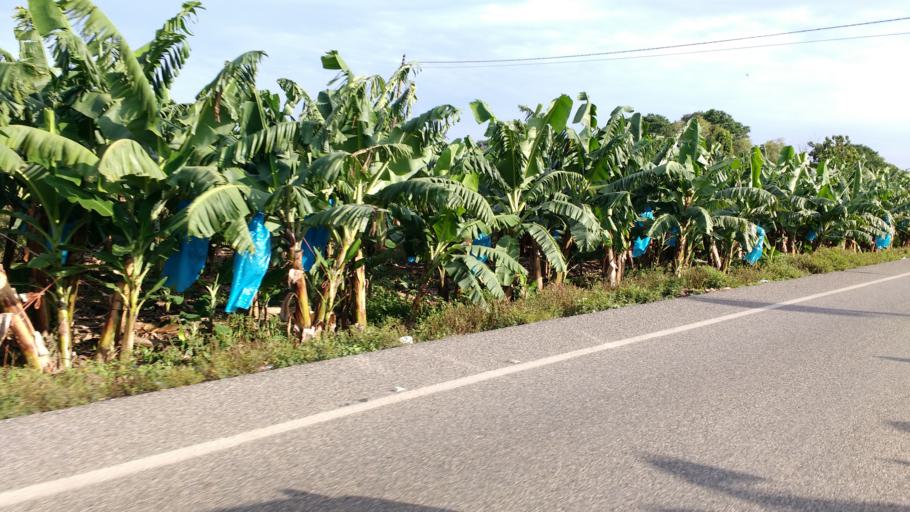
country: MX
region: Tabasco
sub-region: Teapa
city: Eureka y Belen
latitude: 17.6223
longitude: -92.9626
